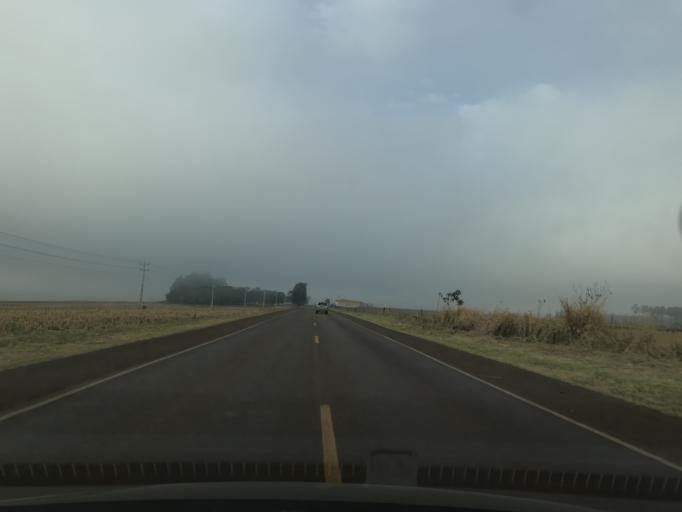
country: BR
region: Parana
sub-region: Toledo
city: Toledo
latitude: -24.6772
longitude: -53.6963
